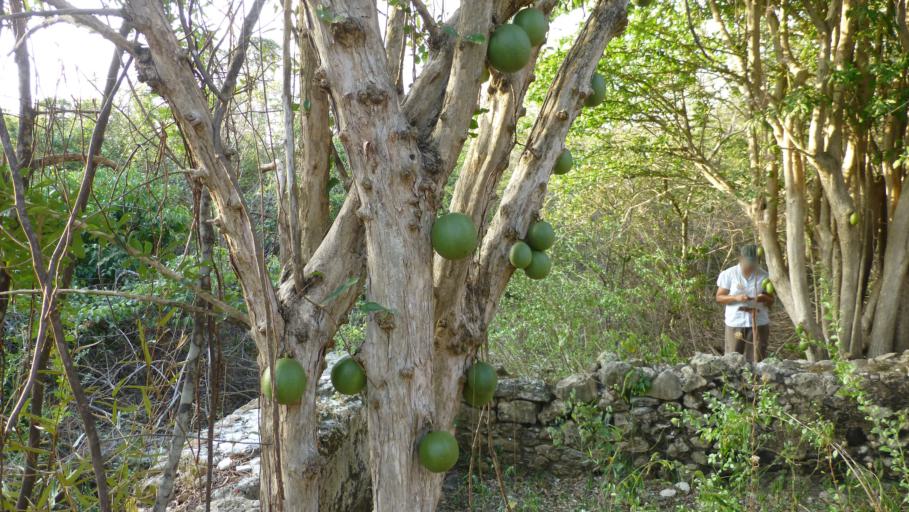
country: CW
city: Sint Michiel Liber
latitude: 12.1637
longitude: -68.9978
